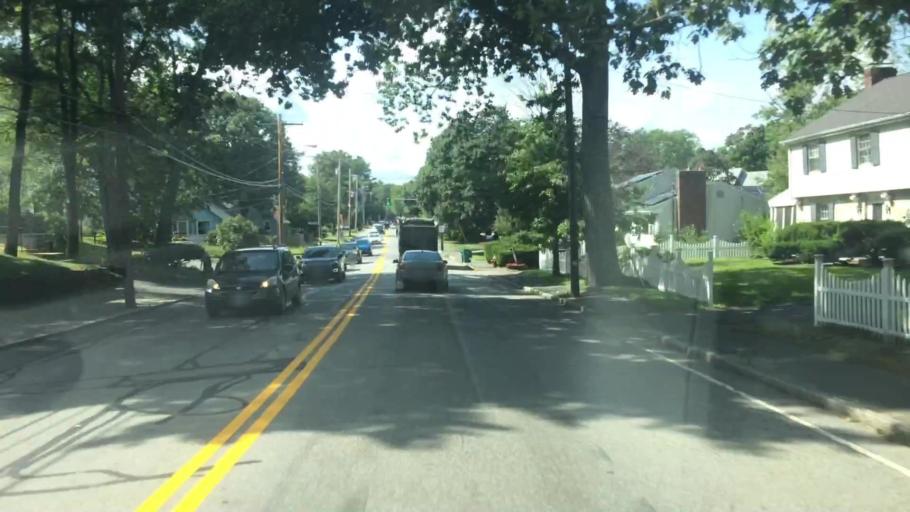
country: US
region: Massachusetts
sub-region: Essex County
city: South Peabody
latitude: 42.5087
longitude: -70.9868
